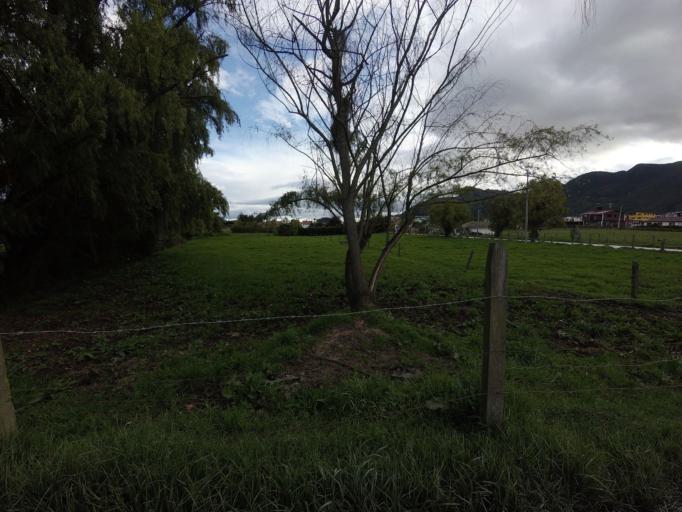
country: CO
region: Cundinamarca
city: Tabio
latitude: 4.9260
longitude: -74.0904
